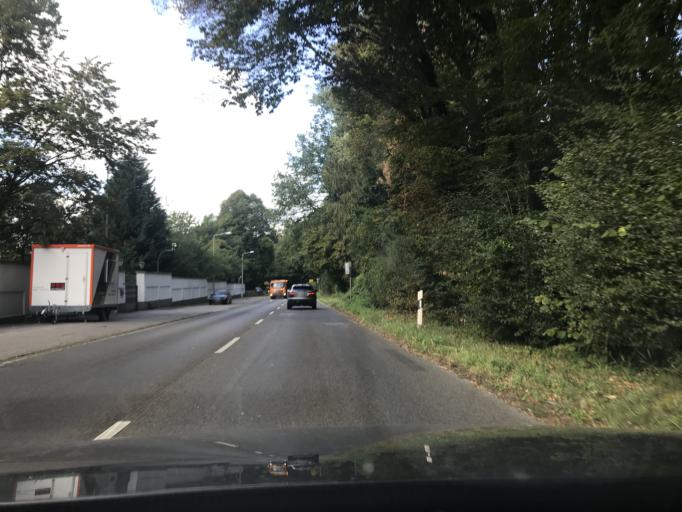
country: DE
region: North Rhine-Westphalia
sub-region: Regierungsbezirk Dusseldorf
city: Erkrath
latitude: 51.2265
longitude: 6.8928
